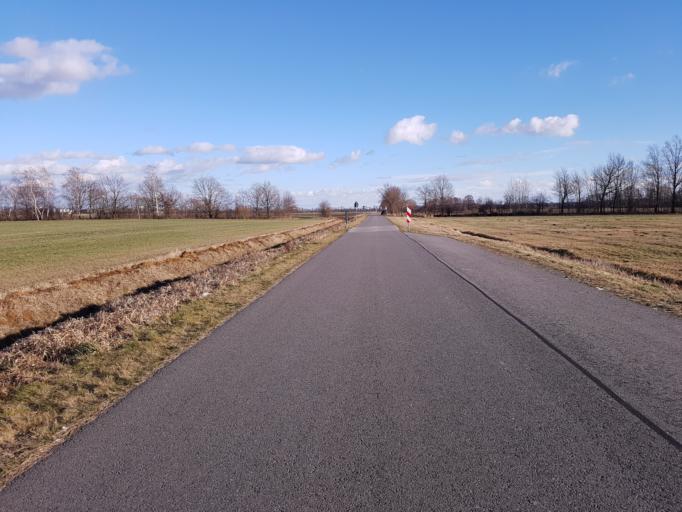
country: DE
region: Brandenburg
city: Groden
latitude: 51.4131
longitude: 13.5740
